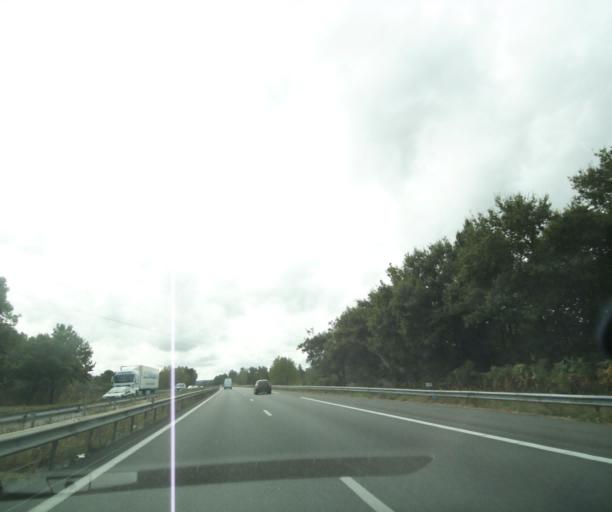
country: FR
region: Poitou-Charentes
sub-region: Departement de la Charente-Maritime
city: Saint-Genis-de-Saintonge
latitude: 45.4601
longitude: -0.6185
